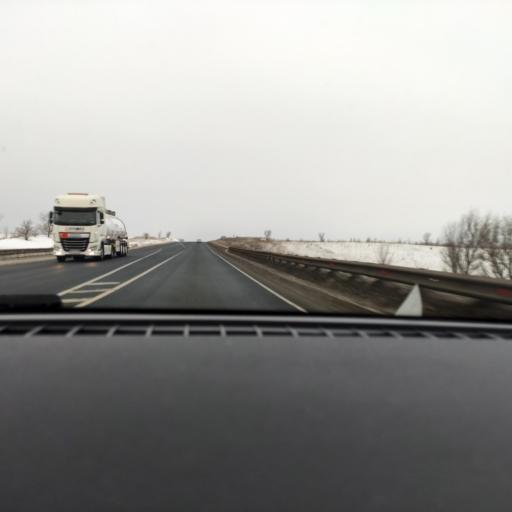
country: RU
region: Samara
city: Novosemeykino
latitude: 53.4014
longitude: 50.4017
